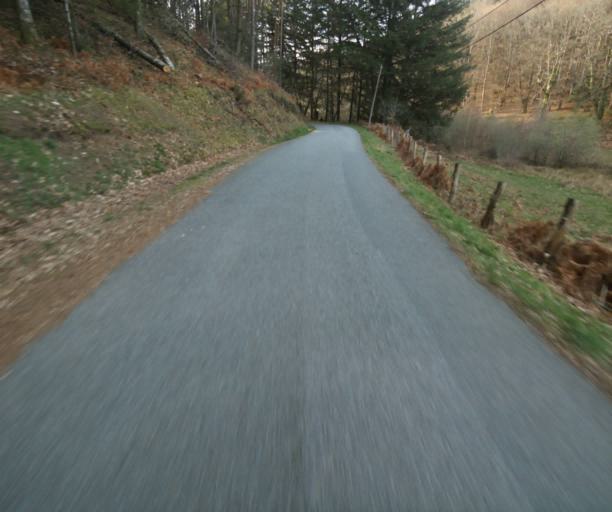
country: FR
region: Limousin
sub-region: Departement de la Correze
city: Correze
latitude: 45.3827
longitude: 1.8568
